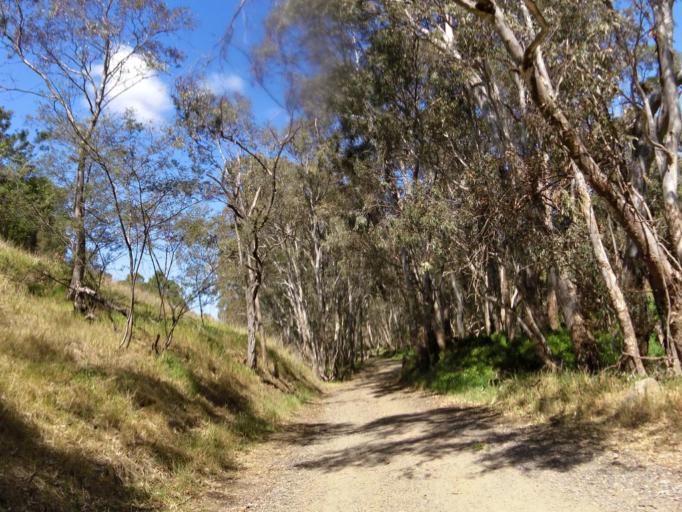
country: AU
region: Victoria
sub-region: Brimbank
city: Albion
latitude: -37.7579
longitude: 144.8491
